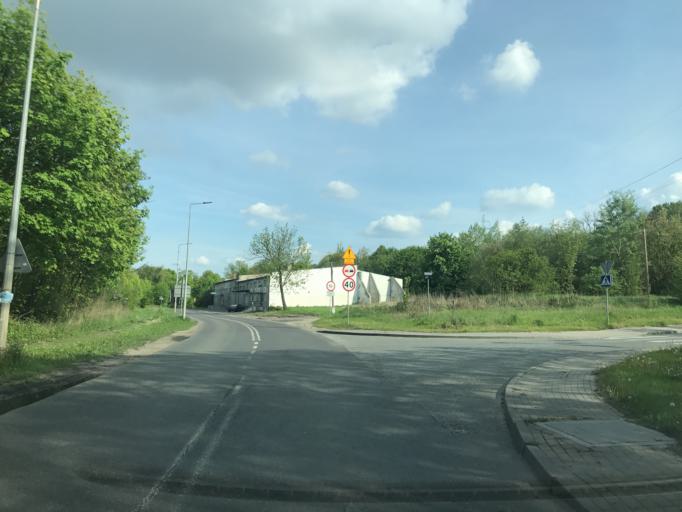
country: PL
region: Kujawsko-Pomorskie
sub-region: Bydgoszcz
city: Fordon
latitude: 53.1139
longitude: 18.1095
